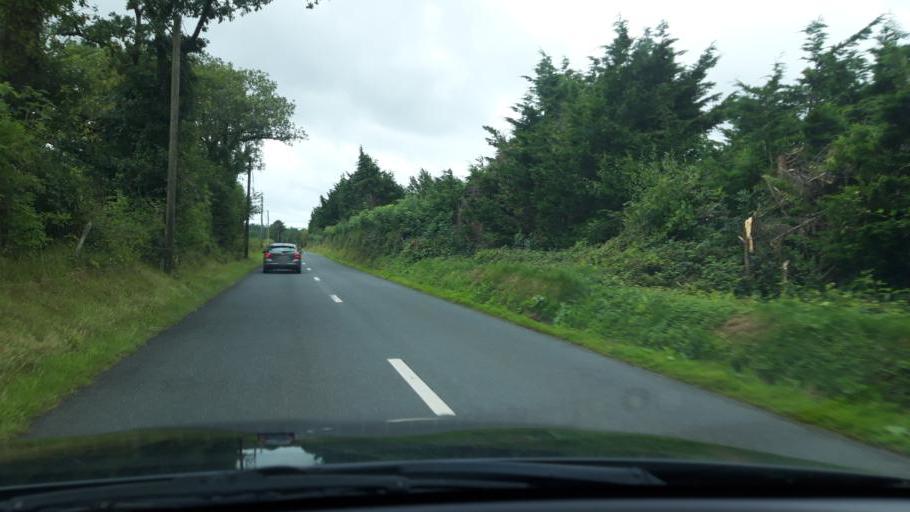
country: IE
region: Munster
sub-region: County Cork
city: Youghal
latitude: 52.1579
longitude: -7.8412
